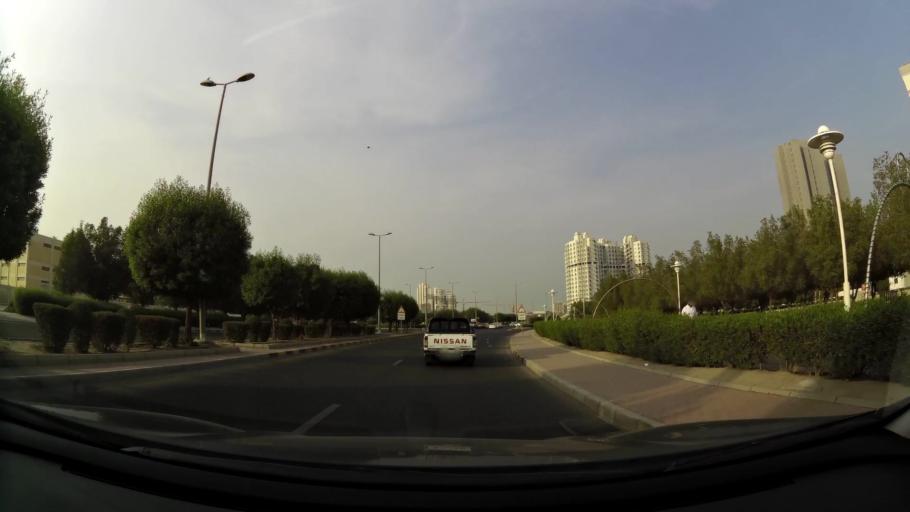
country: KW
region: Mubarak al Kabir
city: Sabah as Salim
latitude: 29.2556
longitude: 48.0783
